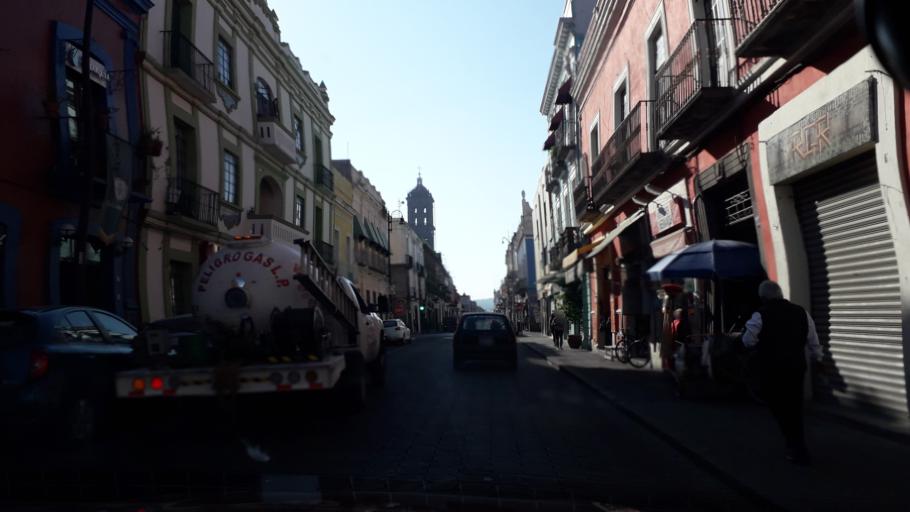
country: MX
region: Puebla
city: Puebla
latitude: 19.0440
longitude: -98.2016
